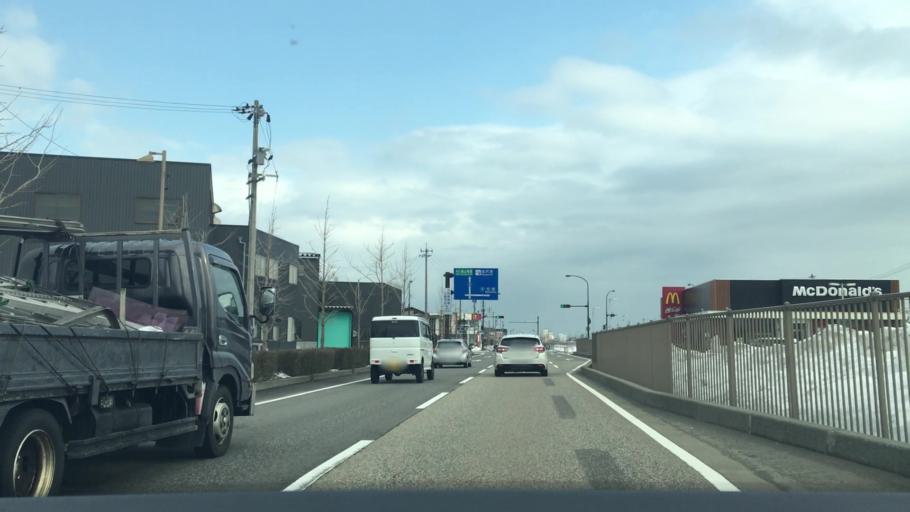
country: JP
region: Ishikawa
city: Nonoichi
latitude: 36.5633
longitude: 136.5802
